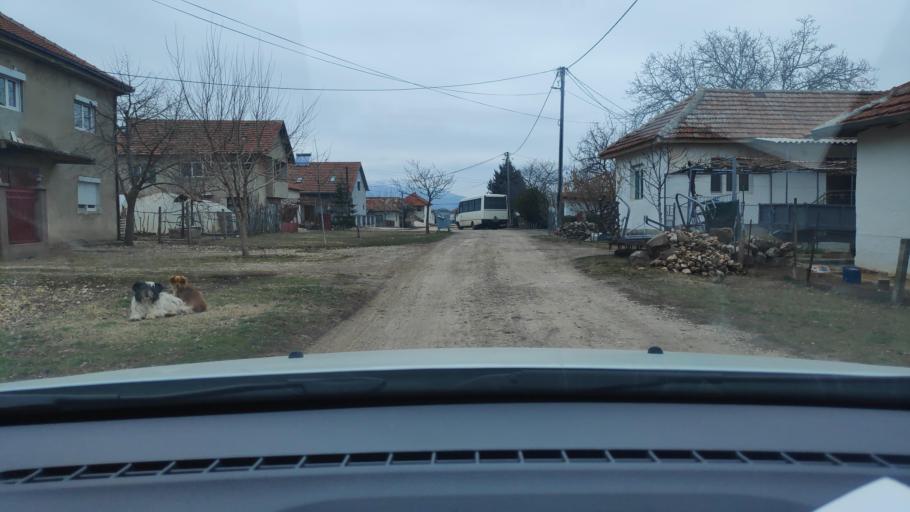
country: MK
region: Opstina Lipkovo
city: Matejche
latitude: 42.0851
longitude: 21.6218
